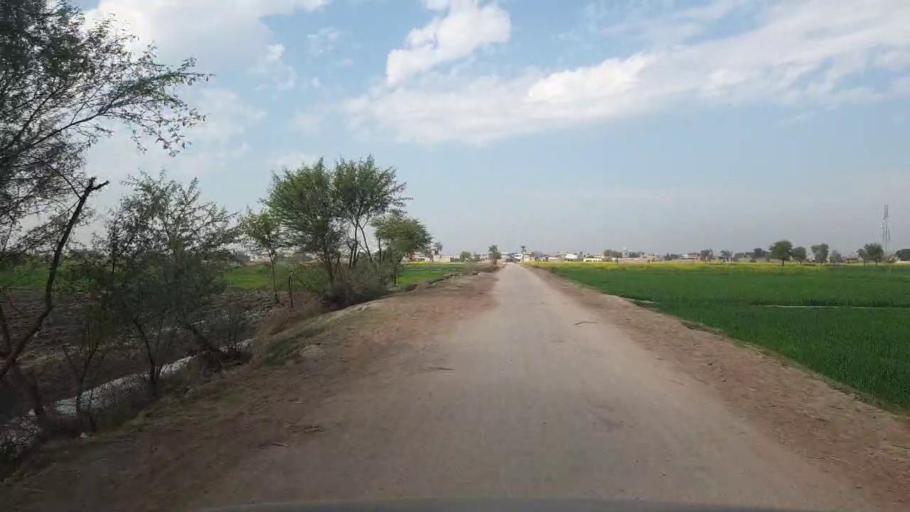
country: PK
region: Sindh
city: Sakrand
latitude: 26.0078
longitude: 68.4121
